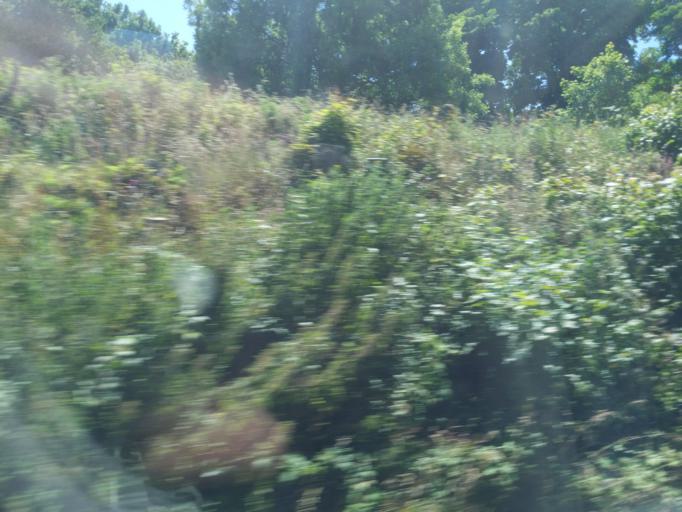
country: GB
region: England
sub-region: Cornwall
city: Saint Stephen
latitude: 50.3274
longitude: -4.8642
